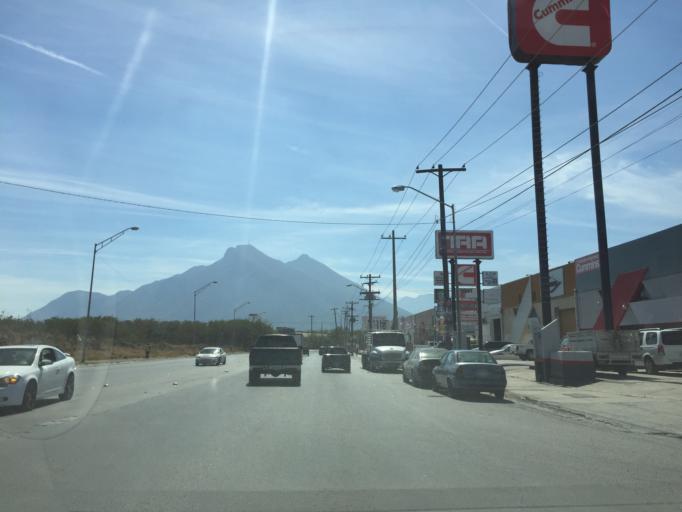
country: MX
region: Nuevo Leon
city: Guadalupe
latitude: 25.7006
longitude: -100.2399
